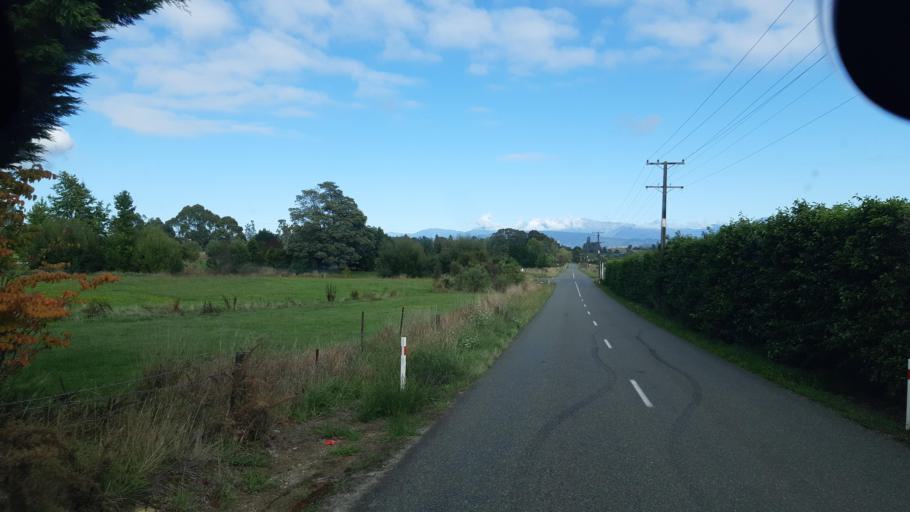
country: NZ
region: Tasman
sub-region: Tasman District
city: Mapua
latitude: -41.2413
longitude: 173.0343
